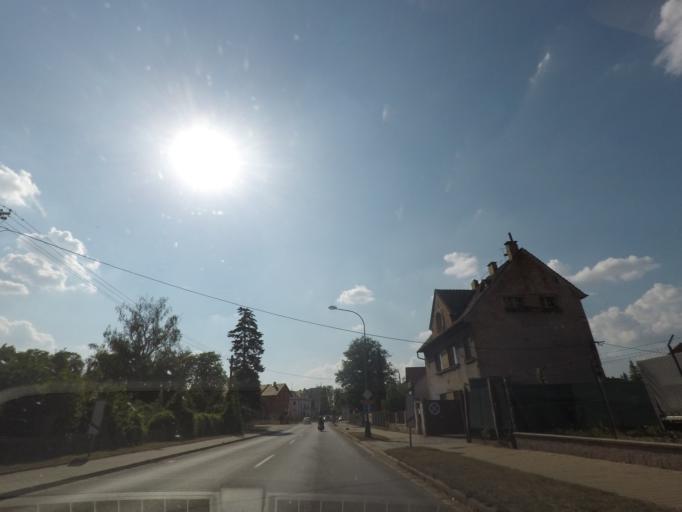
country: CZ
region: Kralovehradecky
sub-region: Okres Nachod
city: Jaromer
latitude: 50.3452
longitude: 15.9204
